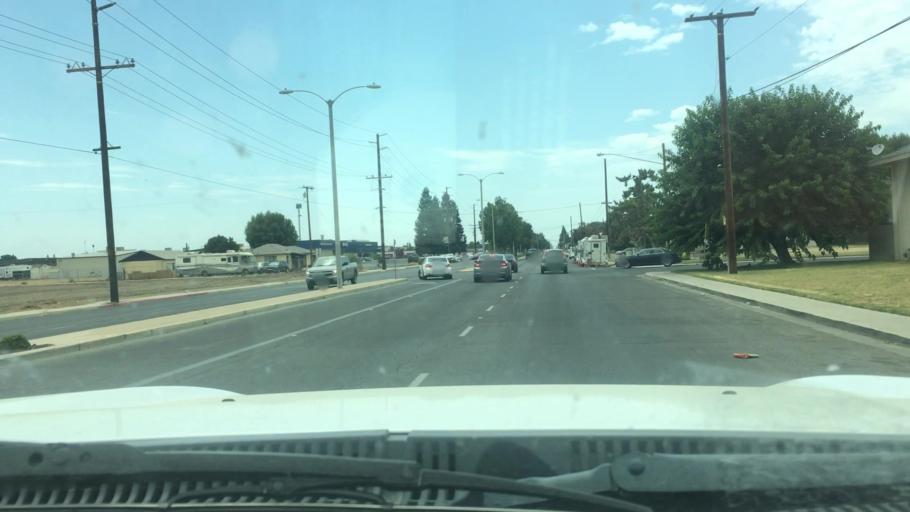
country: US
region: California
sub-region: Tulare County
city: Porterville
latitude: 36.0659
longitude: -119.0568
